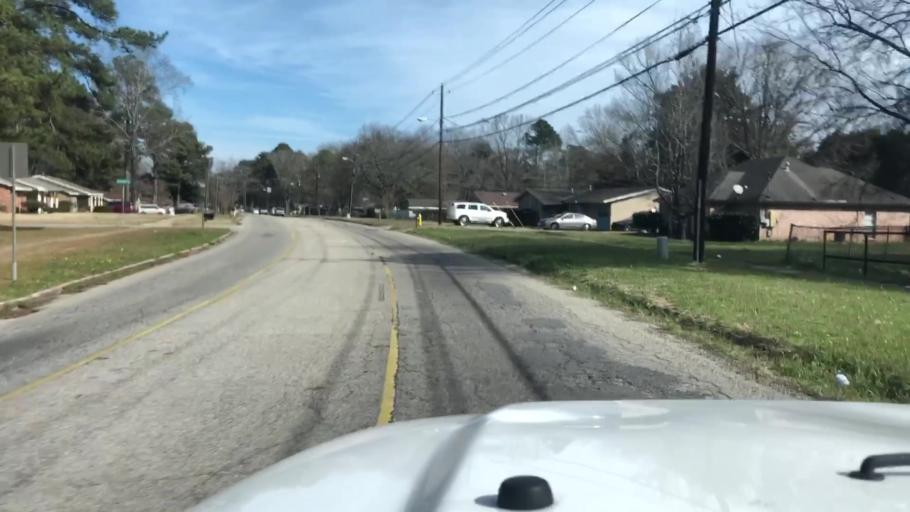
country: US
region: Alabama
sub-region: Elmore County
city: Blue Ridge
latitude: 32.3936
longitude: -86.1948
